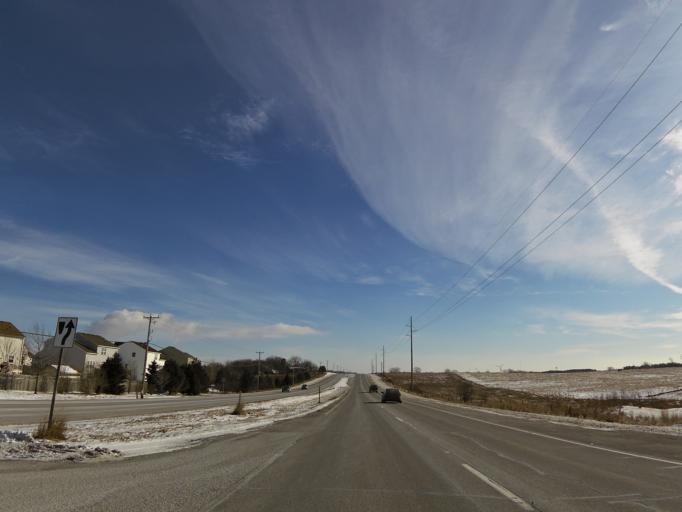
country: US
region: Minnesota
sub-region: Dakota County
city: Rosemount
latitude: 44.7391
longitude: -93.1004
